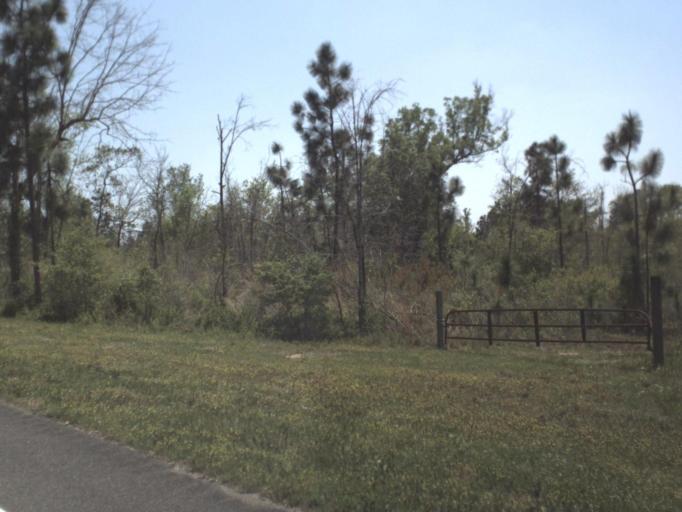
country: US
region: Alabama
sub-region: Escambia County
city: East Brewton
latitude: 30.9182
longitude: -87.0457
